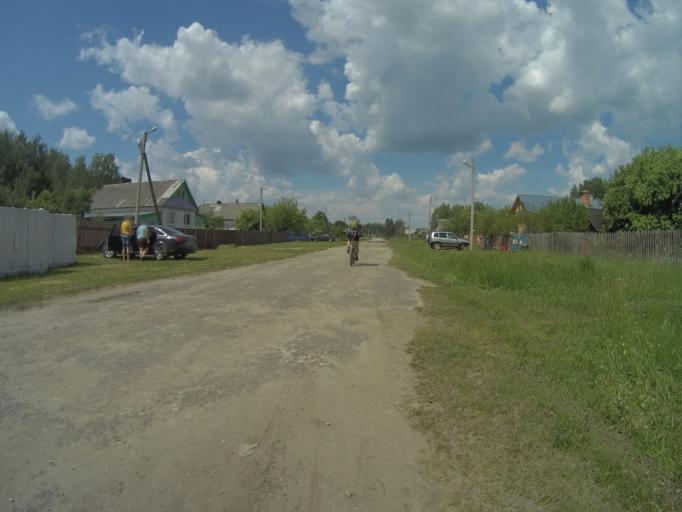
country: RU
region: Vladimir
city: Raduzhnyy
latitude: 55.9922
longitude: 40.2164
